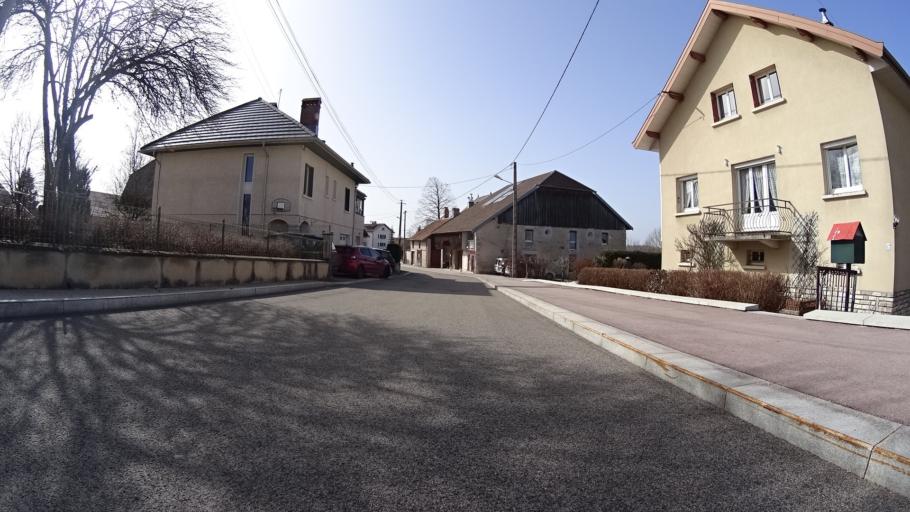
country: FR
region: Franche-Comte
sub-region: Departement du Doubs
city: Frasne
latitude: 46.8552
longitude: 6.1553
